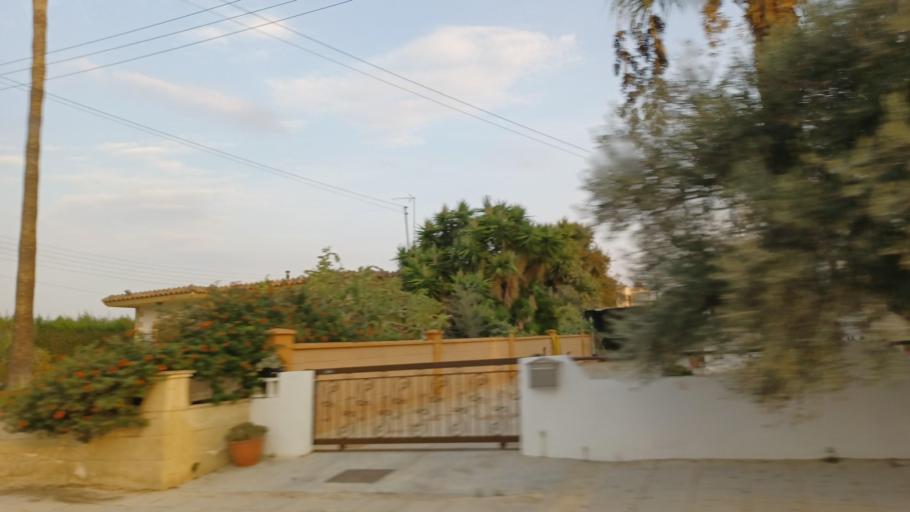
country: CY
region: Lefkosia
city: Lympia
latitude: 34.9948
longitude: 33.4692
